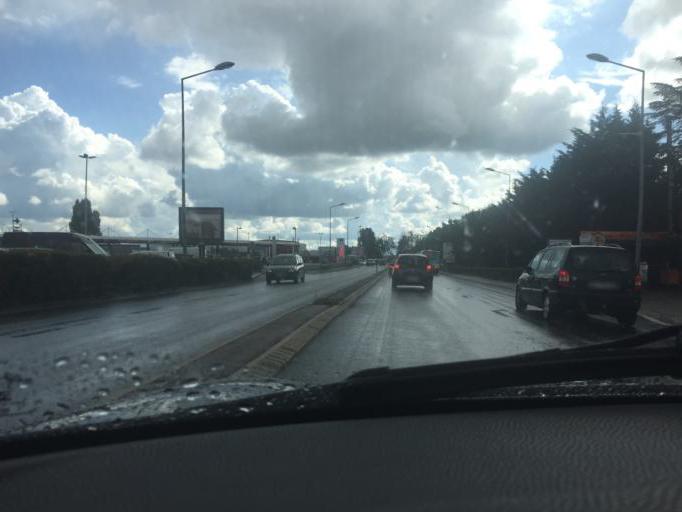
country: FR
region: Ile-de-France
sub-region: Departement du Val-de-Marne
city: Ormesson-sur-Marne
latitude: 48.7939
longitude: 2.5526
